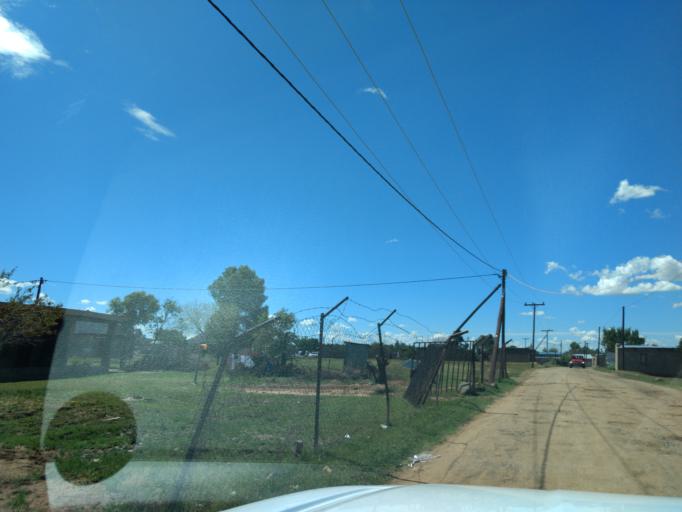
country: LS
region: Maseru
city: Maseru
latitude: -29.3722
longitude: 27.5110
